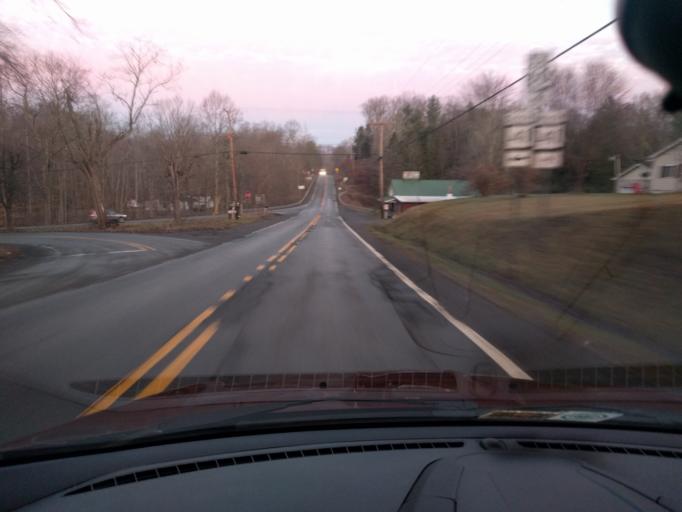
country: US
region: West Virginia
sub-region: Greenbrier County
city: Rainelle
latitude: 38.0202
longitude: -80.9116
